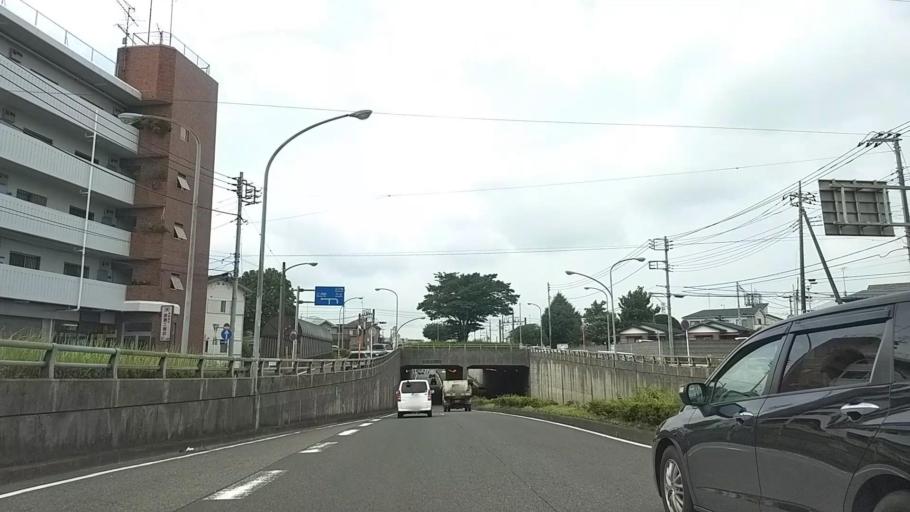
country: JP
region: Kanagawa
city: Minami-rinkan
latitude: 35.4712
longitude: 139.4973
